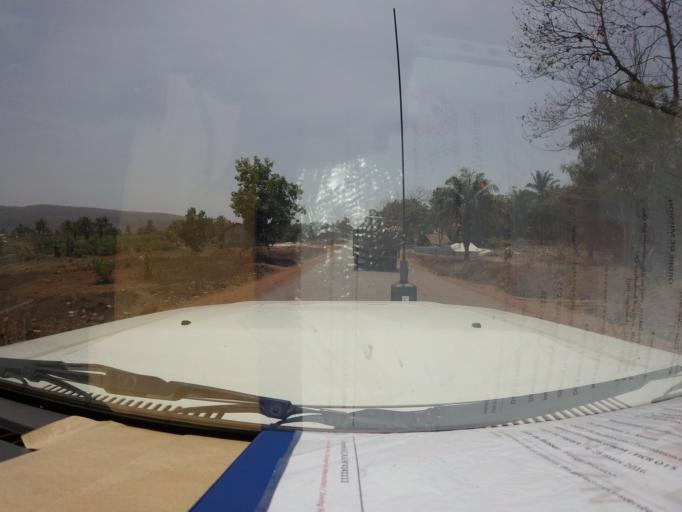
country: GN
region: Kindia
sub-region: Coyah
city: Coyah
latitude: 9.8011
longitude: -13.2859
